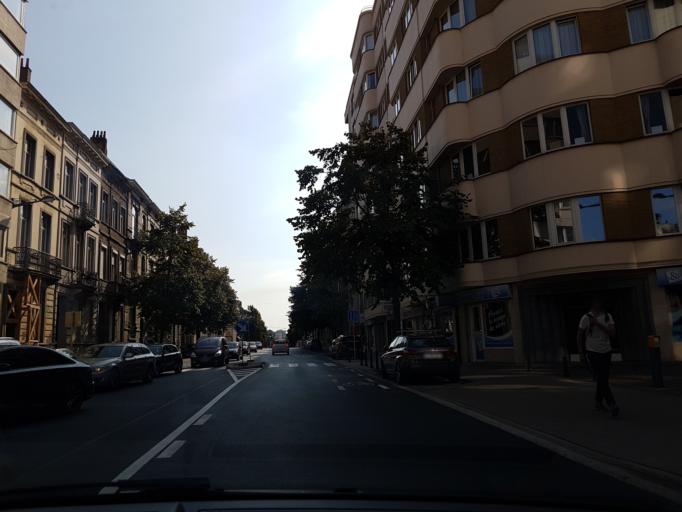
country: BE
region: Brussels Capital
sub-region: Bruxelles-Capitale
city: Brussels
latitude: 50.8389
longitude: 4.3858
